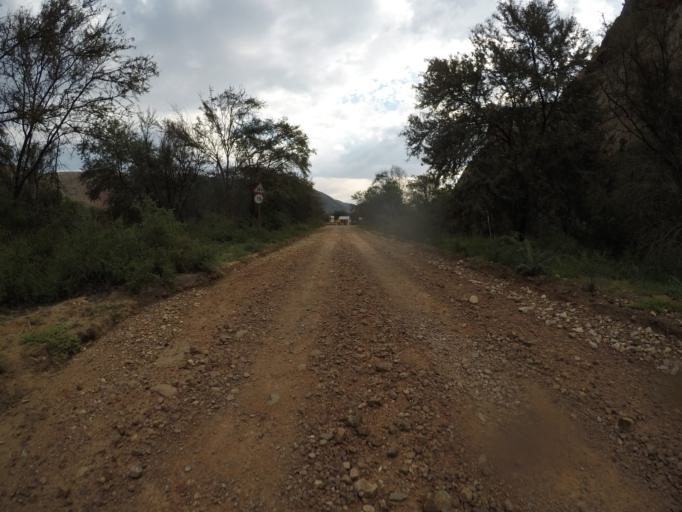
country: ZA
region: Eastern Cape
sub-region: Cacadu District Municipality
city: Kareedouw
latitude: -33.6037
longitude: 24.2011
